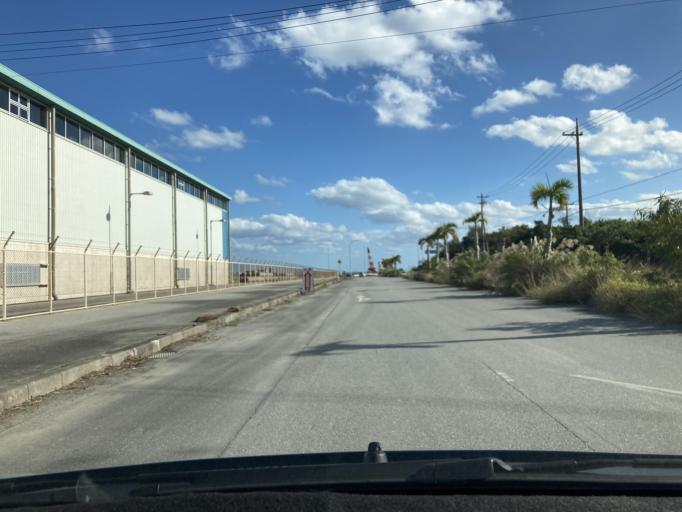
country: JP
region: Okinawa
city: Katsuren-haebaru
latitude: 26.3293
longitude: 127.8559
